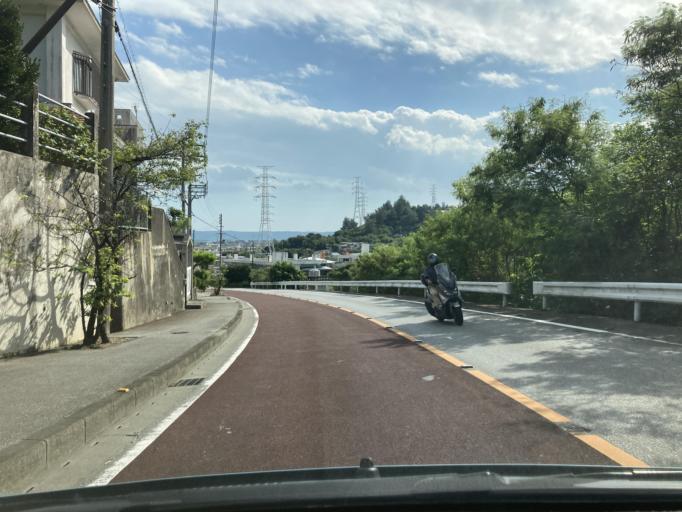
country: JP
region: Okinawa
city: Ginowan
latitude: 26.2573
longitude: 127.7839
